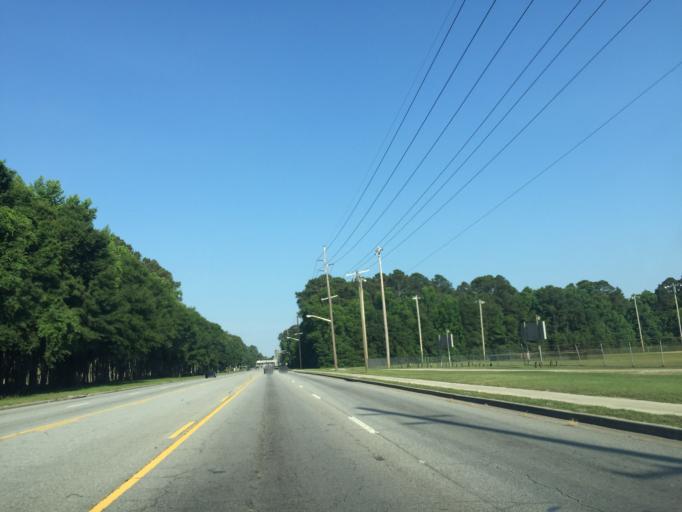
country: US
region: Georgia
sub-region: Chatham County
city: Isle of Hope
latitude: 32.0035
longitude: -81.0895
